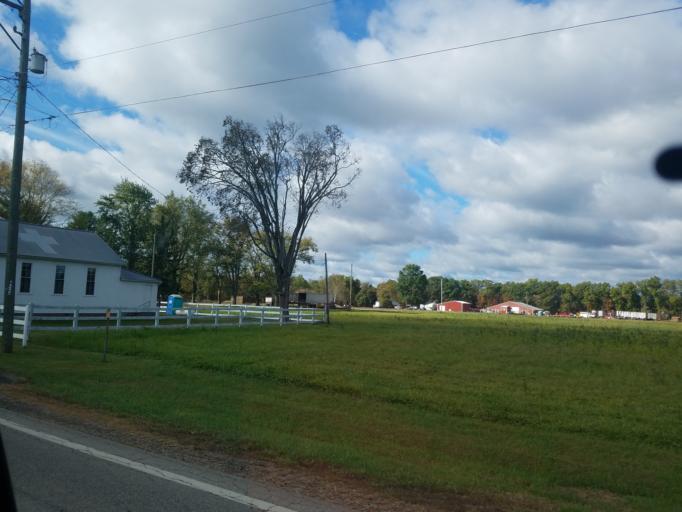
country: US
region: Ohio
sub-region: Vinton County
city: McArthur
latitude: 39.2015
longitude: -82.4805
